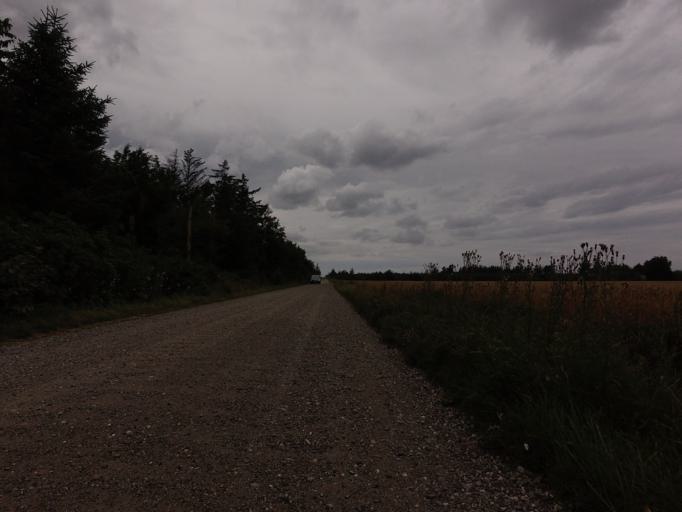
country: DK
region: North Denmark
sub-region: Jammerbugt Kommune
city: Pandrup
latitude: 57.3390
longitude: 9.7030
